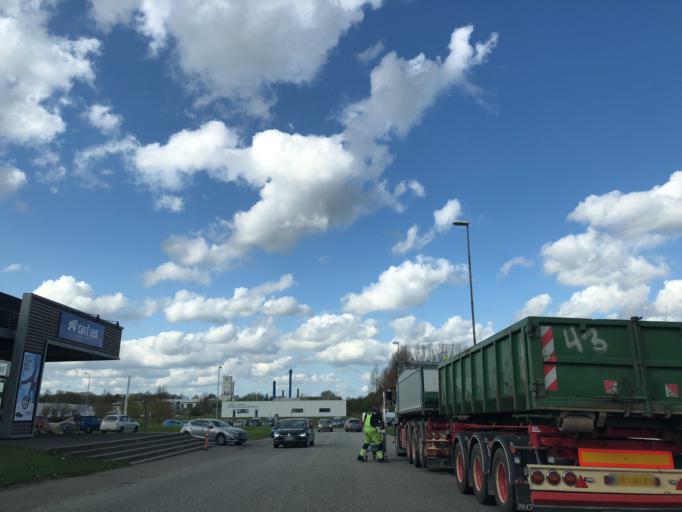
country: DK
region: Zealand
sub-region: Ringsted Kommune
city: Ringsted
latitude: 55.4278
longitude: 11.7908
